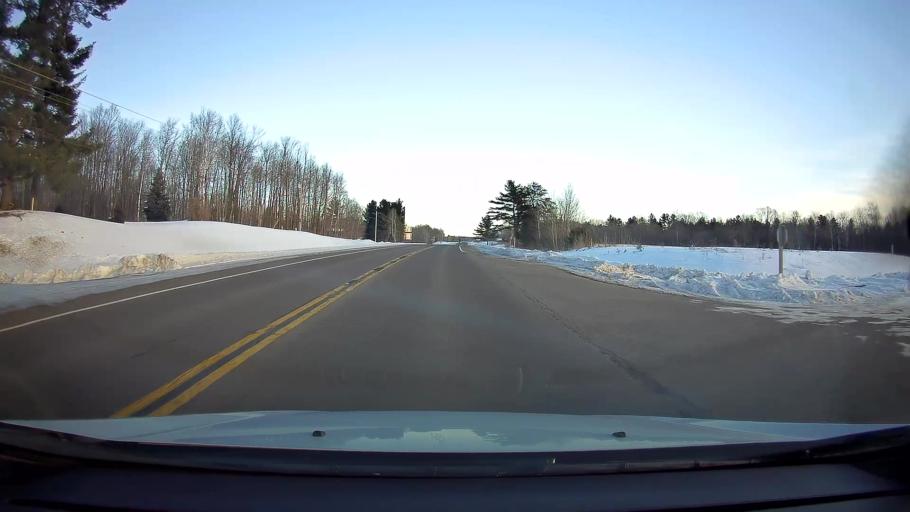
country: US
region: Wisconsin
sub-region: Barron County
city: Cumberland
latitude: 45.6036
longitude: -92.0156
